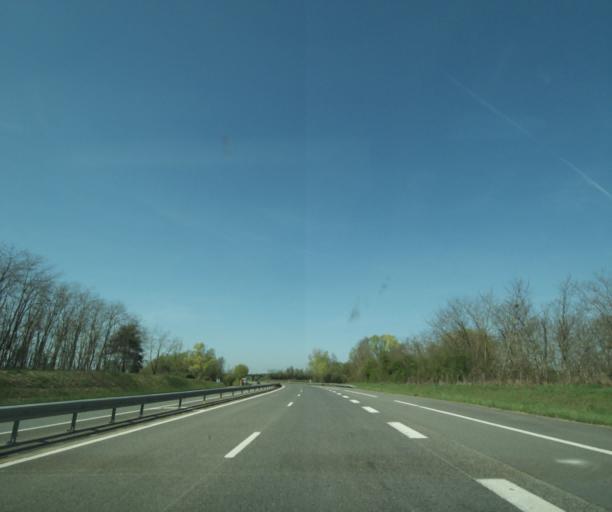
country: FR
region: Auvergne
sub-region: Departement de l'Allier
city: Moulins
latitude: 46.5906
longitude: 3.3374
